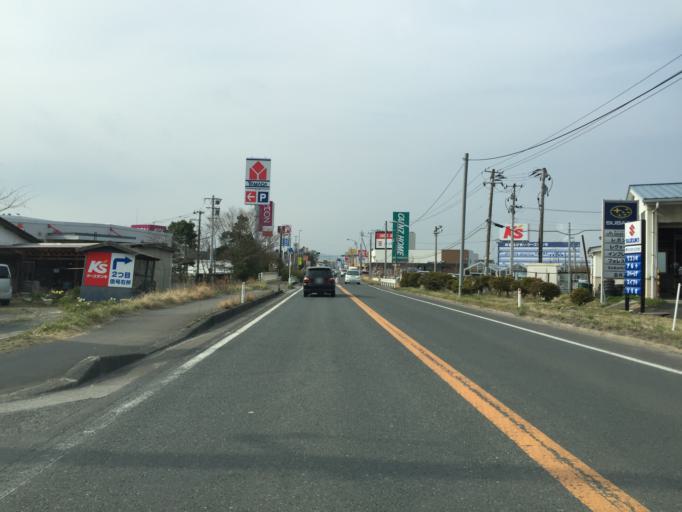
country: JP
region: Miyagi
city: Marumori
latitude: 37.7864
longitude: 140.9330
